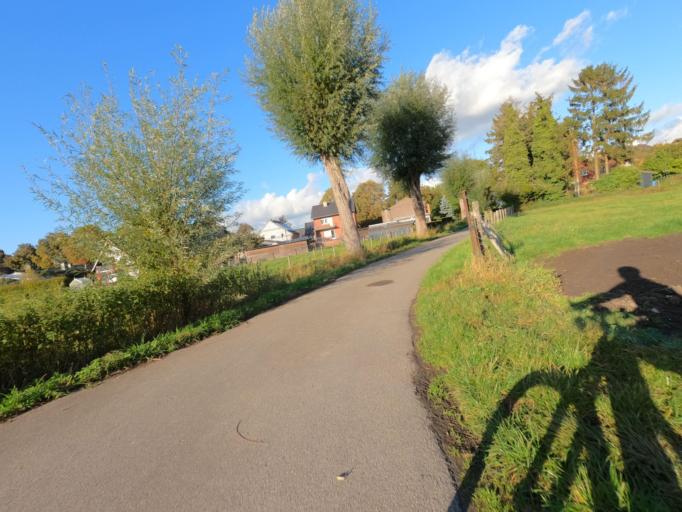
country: DE
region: North Rhine-Westphalia
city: Huckelhoven
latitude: 51.0291
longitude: 6.1783
